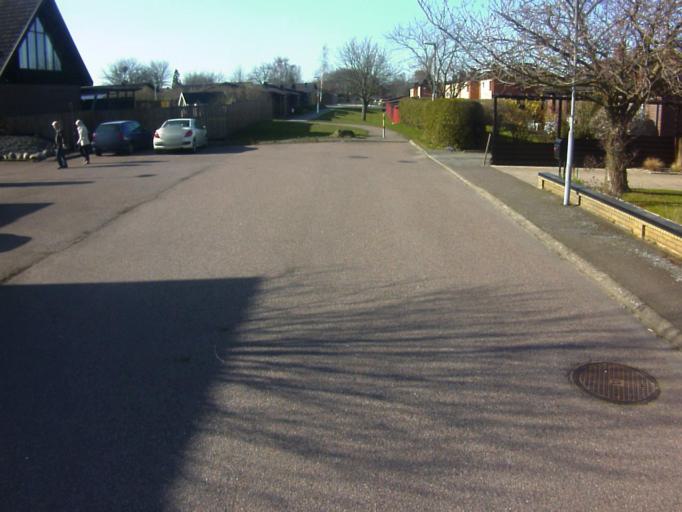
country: SE
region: Skane
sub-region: Kavlinge Kommun
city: Kaevlinge
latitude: 55.7915
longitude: 13.0979
